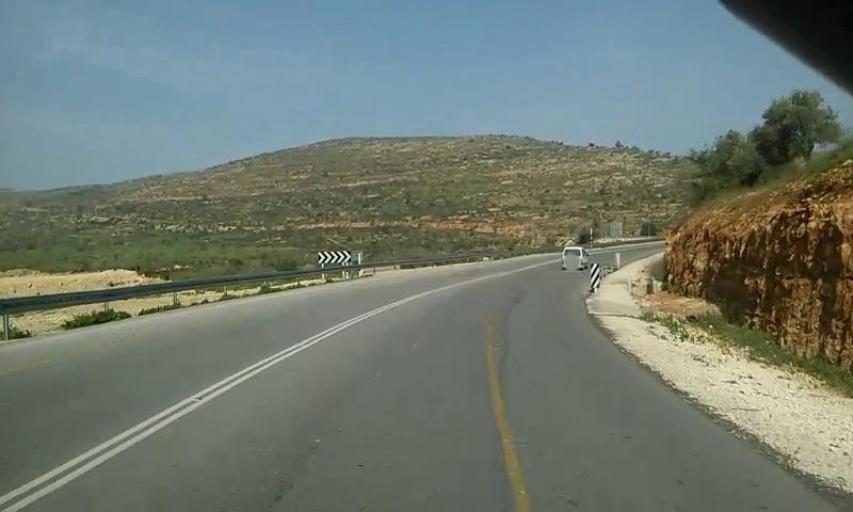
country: PS
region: West Bank
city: `Atarah
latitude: 31.9869
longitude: 35.2277
